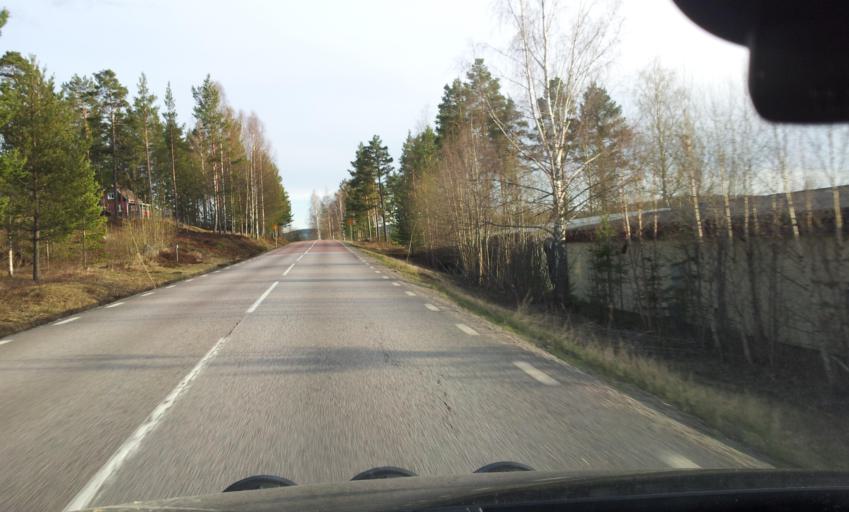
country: SE
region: Vaesternorrland
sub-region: Ange Kommun
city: Ange
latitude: 62.1593
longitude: 15.6770
